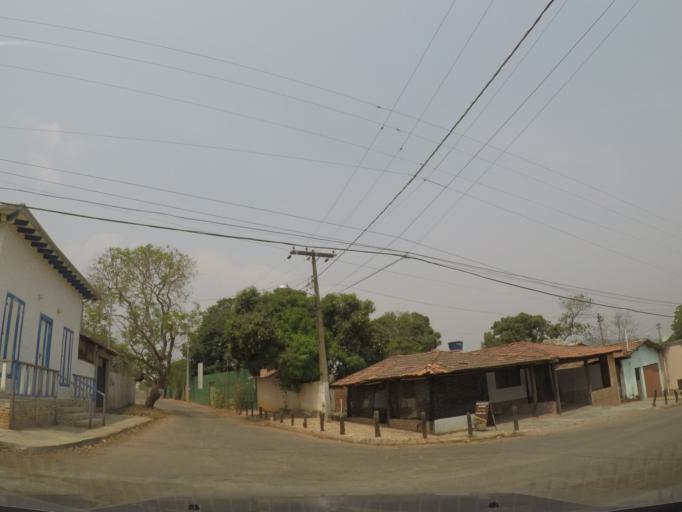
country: BR
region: Goias
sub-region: Pirenopolis
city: Pirenopolis
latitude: -15.8426
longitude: -48.9595
